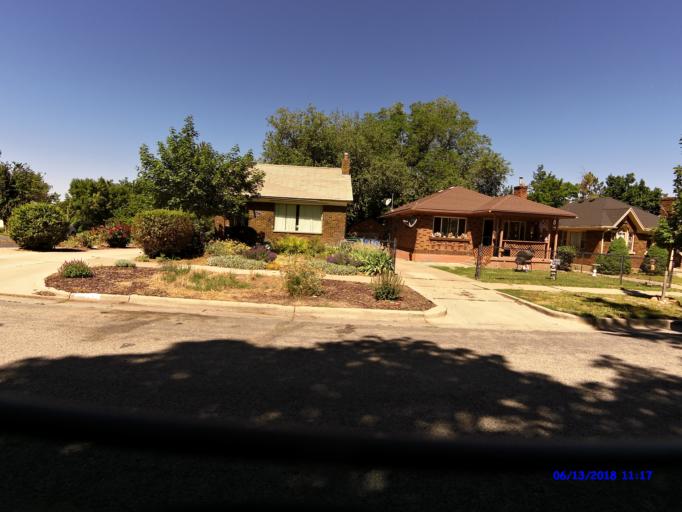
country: US
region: Utah
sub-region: Weber County
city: Ogden
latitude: 41.2122
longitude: -111.9499
